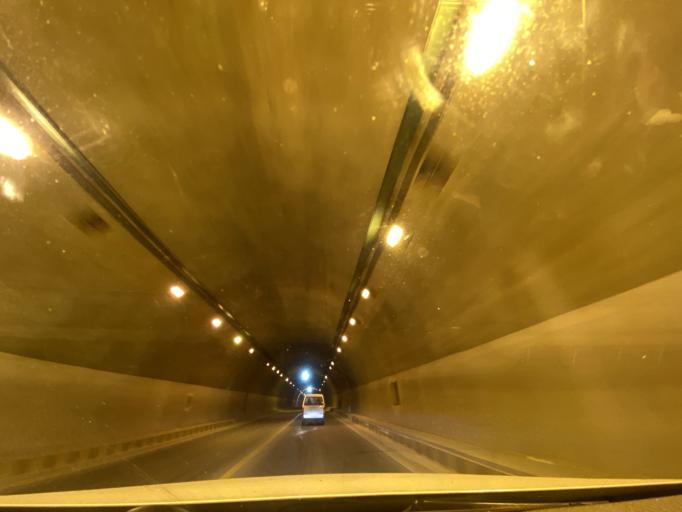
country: CN
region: Hainan
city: Tiandu
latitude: 18.3108
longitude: 109.5905
